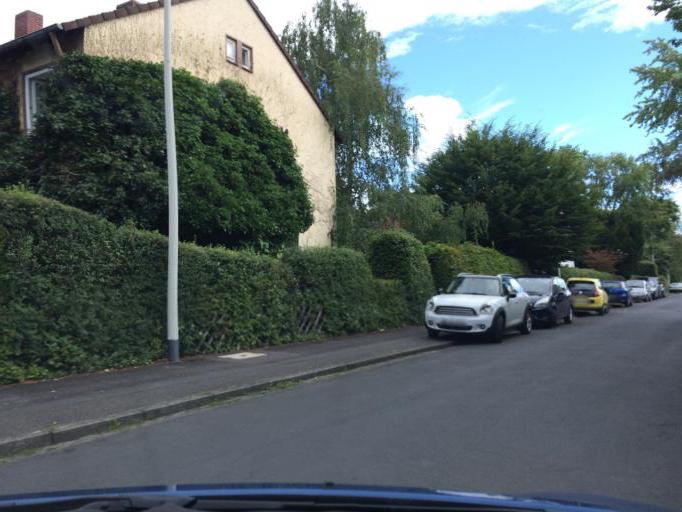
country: DE
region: North Rhine-Westphalia
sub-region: Regierungsbezirk Koln
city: Konigswinter
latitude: 50.6938
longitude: 7.1509
